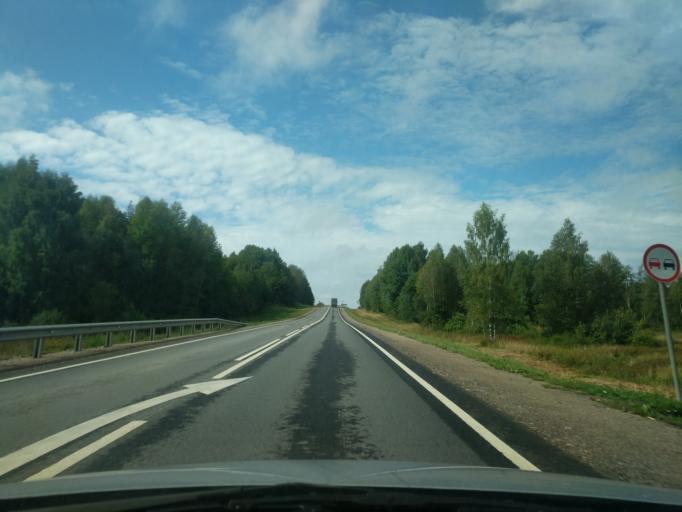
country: RU
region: Kostroma
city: Sudislavl'
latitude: 57.8394
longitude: 41.8506
